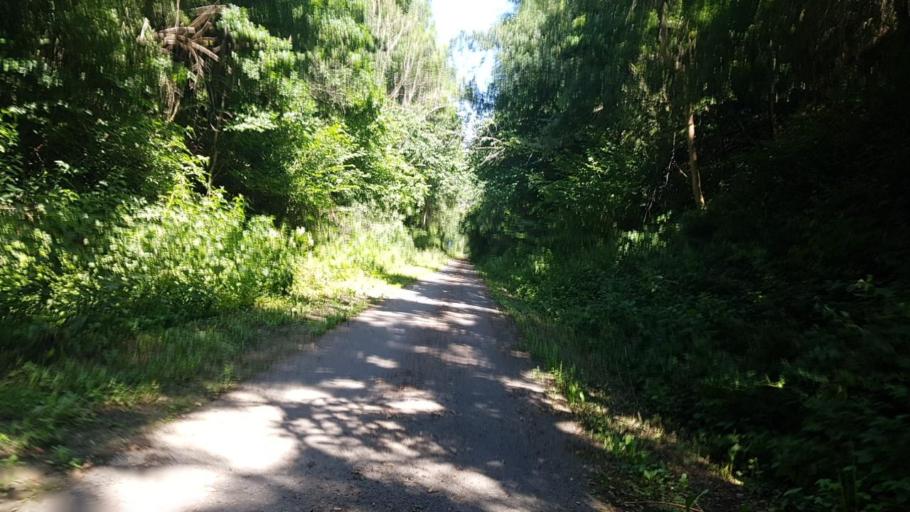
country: BE
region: Wallonia
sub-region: Province du Hainaut
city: Beaumont
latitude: 50.1963
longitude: 4.2259
